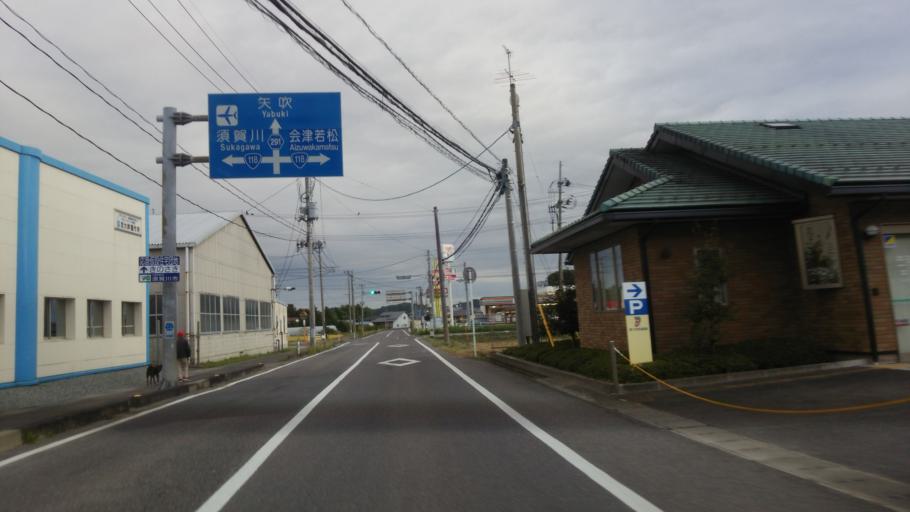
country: JP
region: Fukushima
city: Sukagawa
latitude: 37.2802
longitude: 140.2727
